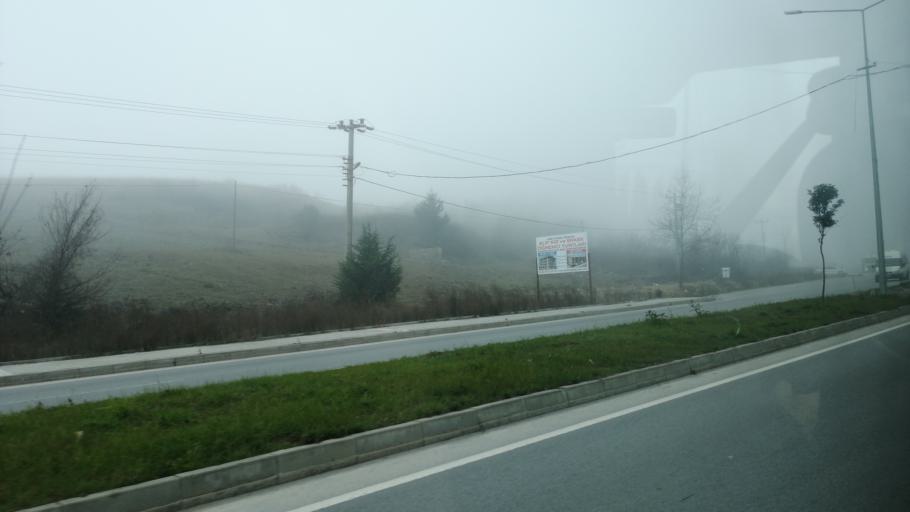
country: TR
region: Yalova
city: Kadikoy
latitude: 40.6488
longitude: 29.2290
